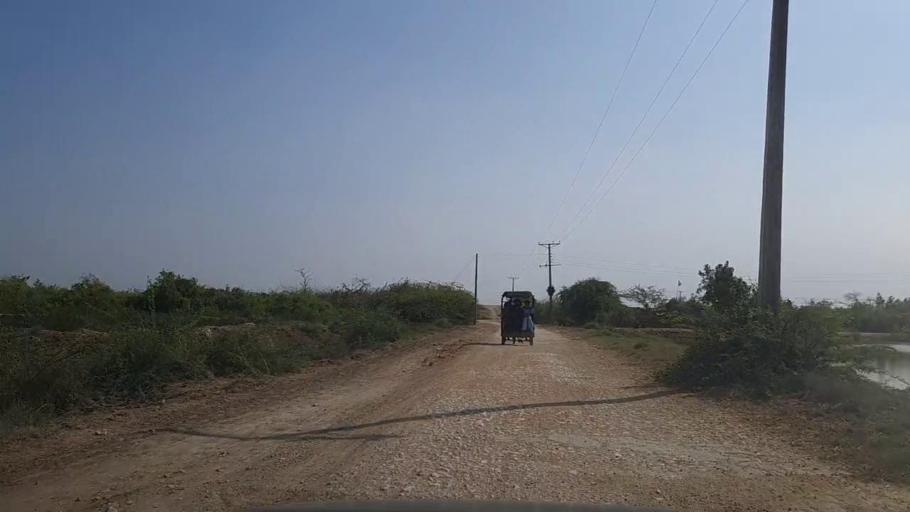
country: PK
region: Sindh
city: Thatta
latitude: 24.5827
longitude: 67.9132
